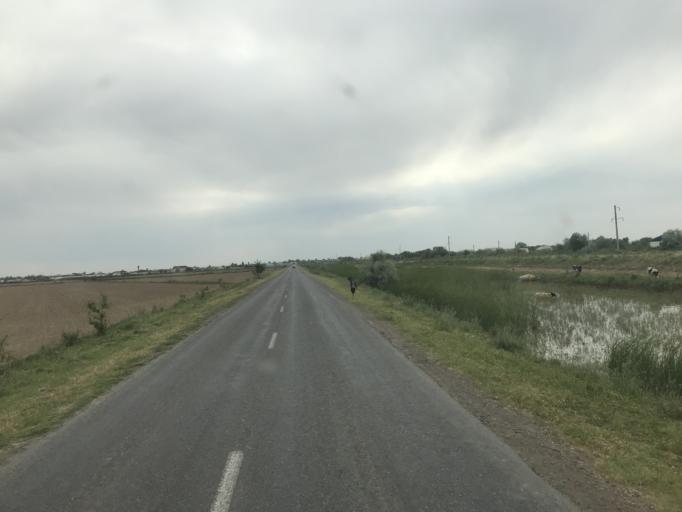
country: KZ
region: Ongtustik Qazaqstan
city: Asykata
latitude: 40.9095
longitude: 68.3873
